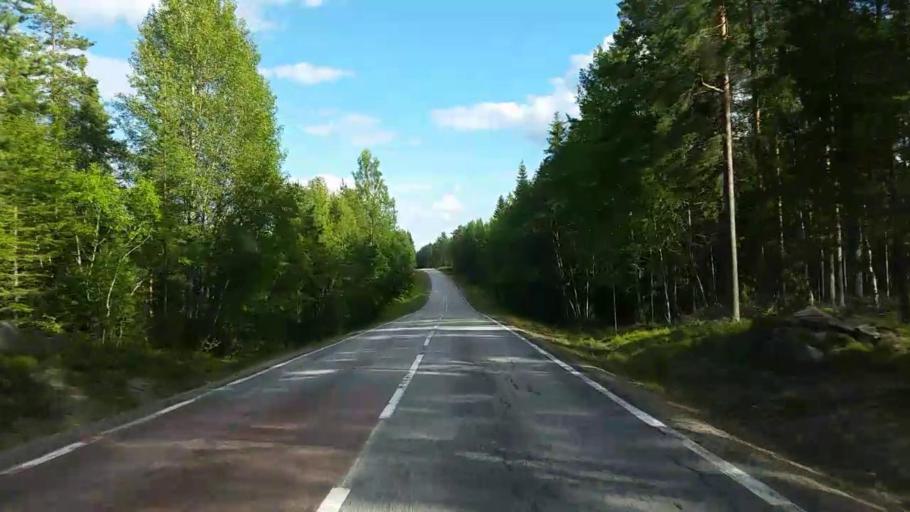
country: SE
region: Gaevleborg
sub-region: Ljusdals Kommun
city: Farila
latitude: 62.0934
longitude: 15.7984
